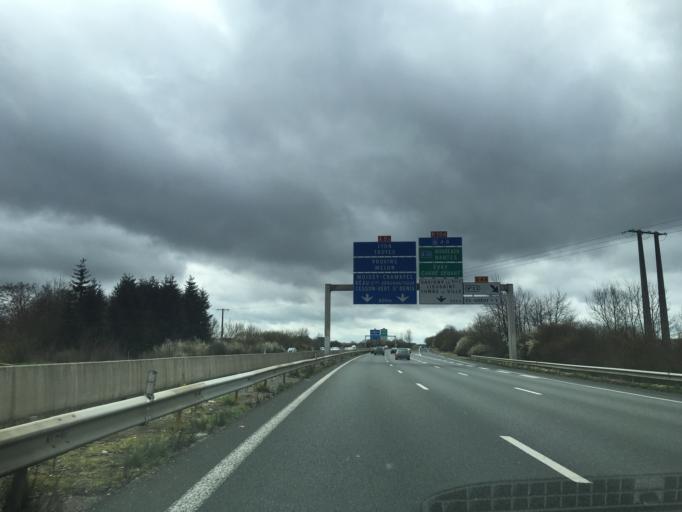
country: FR
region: Ile-de-France
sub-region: Departement de Seine-et-Marne
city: Brie-Comte-Robert
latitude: 48.6621
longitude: 2.6135
